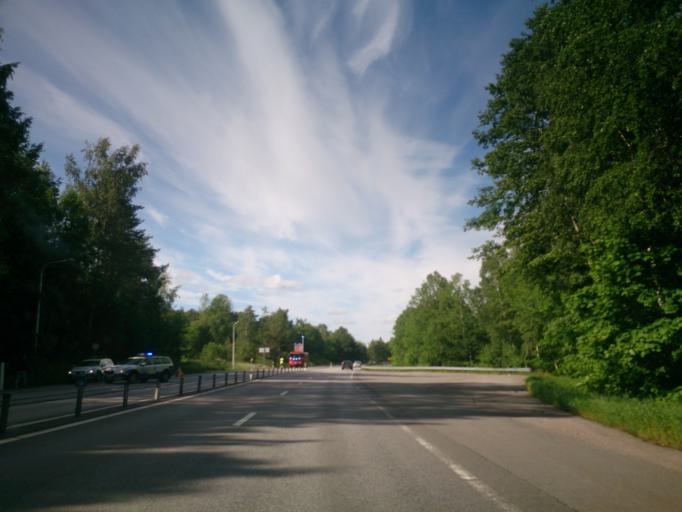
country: SE
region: OEstergoetland
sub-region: Norrkopings Kommun
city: Jursla
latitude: 58.6835
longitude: 16.1496
